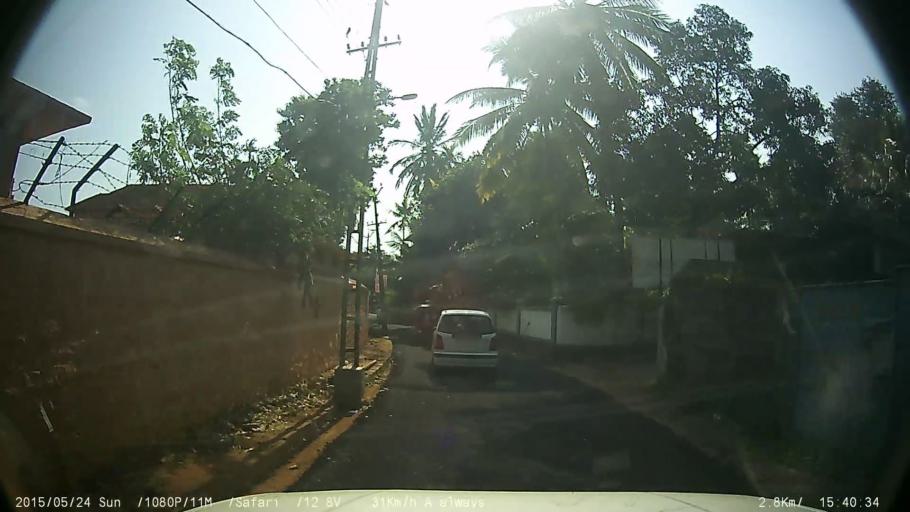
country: IN
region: Kerala
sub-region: Kottayam
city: Changanacheri
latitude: 9.4413
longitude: 76.5466
